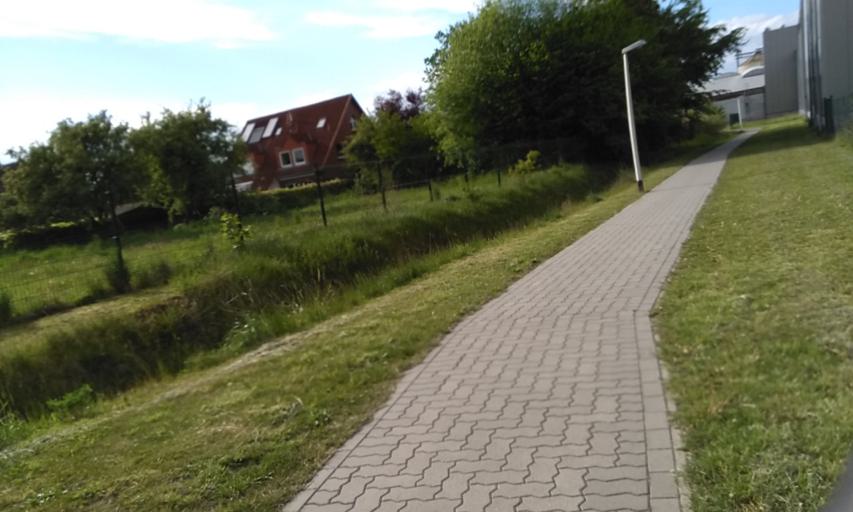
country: DE
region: Lower Saxony
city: Apensen
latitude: 53.4410
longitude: 9.6177
